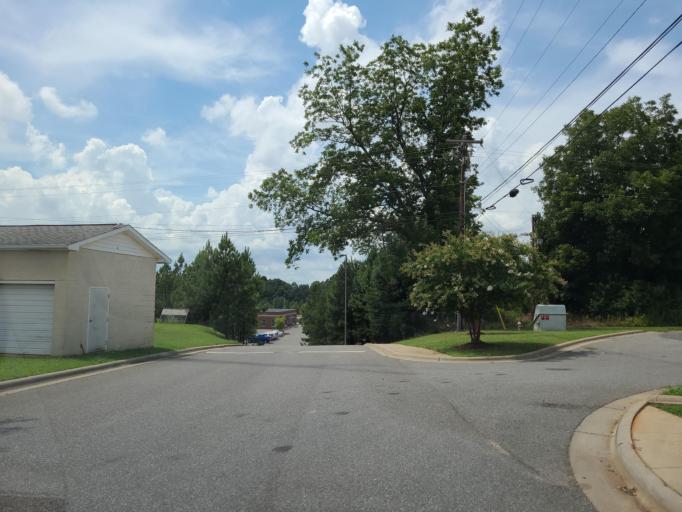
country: US
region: North Carolina
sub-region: Cleveland County
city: Shelby
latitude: 35.2824
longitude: -81.4935
